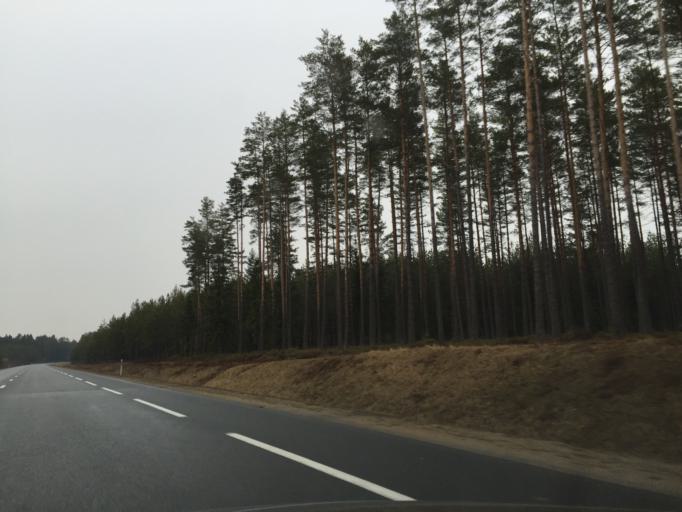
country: LV
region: Saulkrastu
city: Saulkrasti
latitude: 57.2764
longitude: 24.4357
